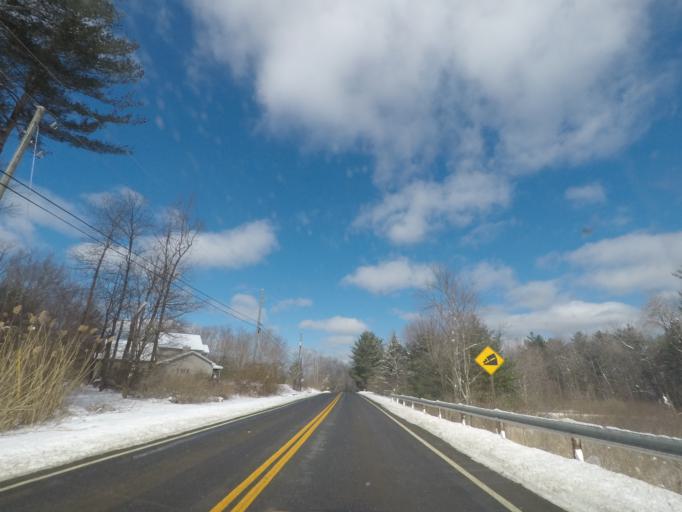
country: US
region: New York
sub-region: Rensselaer County
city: Nassau
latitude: 42.4813
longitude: -73.5206
